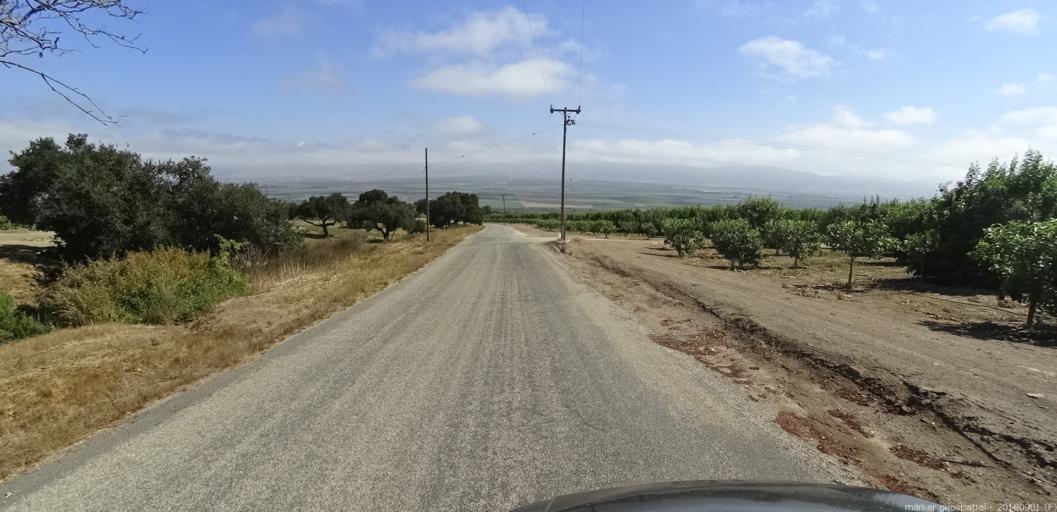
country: US
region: California
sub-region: Monterey County
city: Gonzales
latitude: 36.4442
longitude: -121.4544
